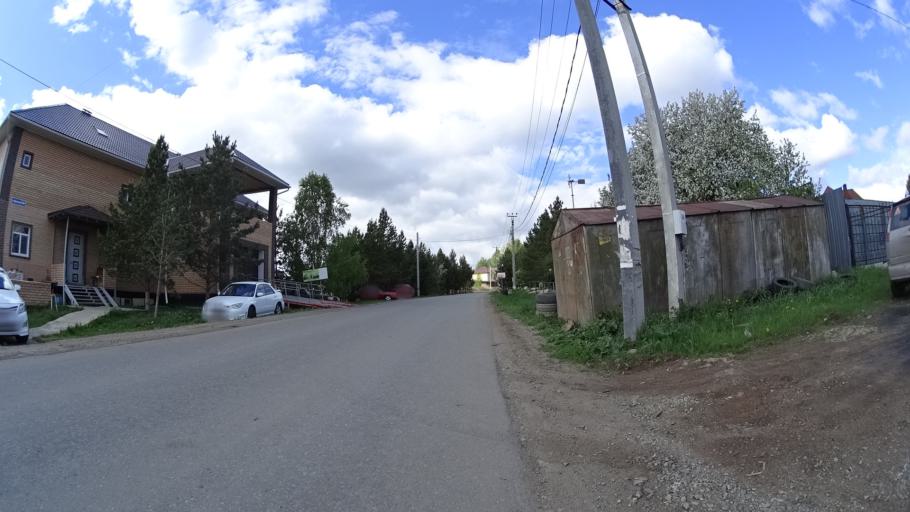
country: RU
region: Chelyabinsk
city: Sargazy
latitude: 55.1562
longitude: 61.2414
